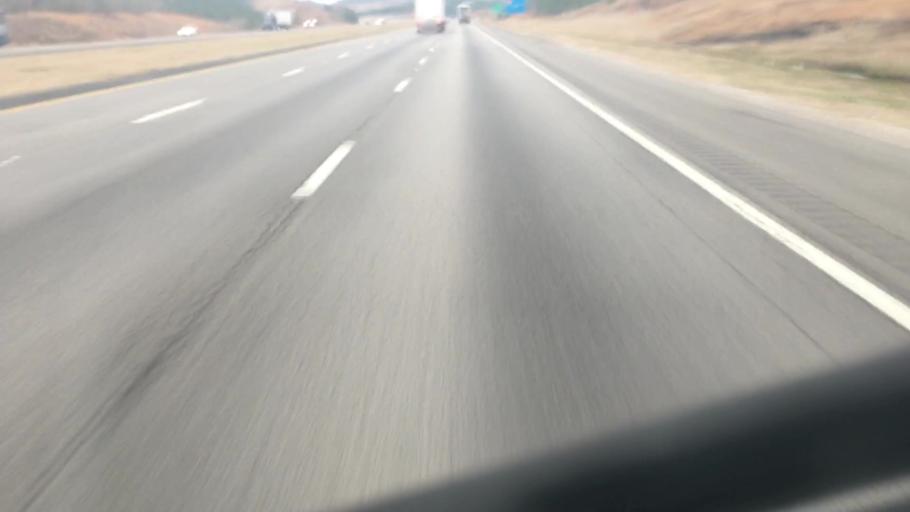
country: US
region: Alabama
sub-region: Walker County
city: Dora
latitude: 33.6726
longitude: -87.0756
